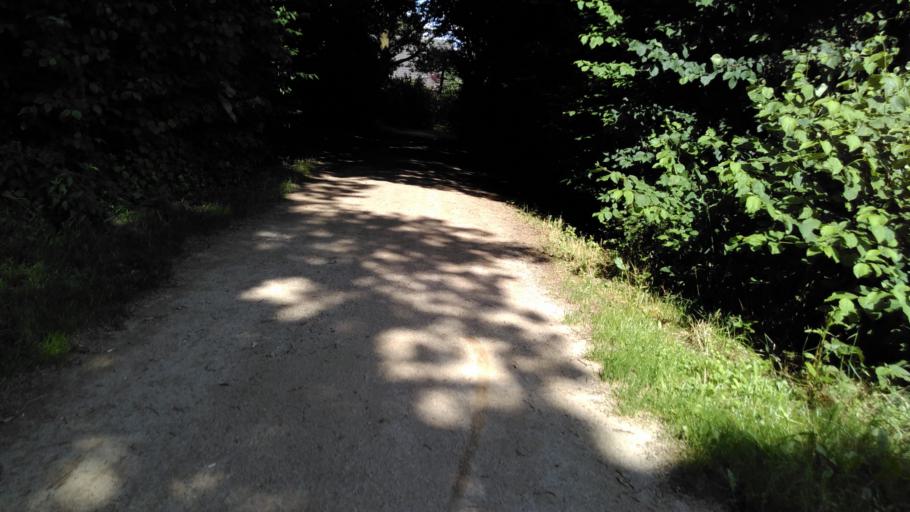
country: DE
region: North Rhine-Westphalia
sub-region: Regierungsbezirk Detmold
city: Verl
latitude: 51.8886
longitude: 8.4814
